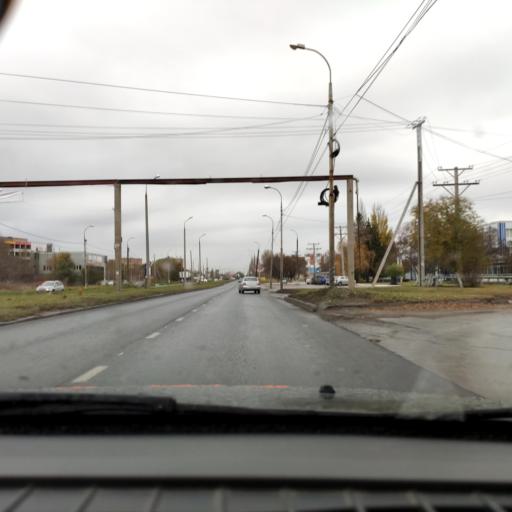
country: RU
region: Samara
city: Tol'yatti
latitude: 53.5601
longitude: 49.3007
